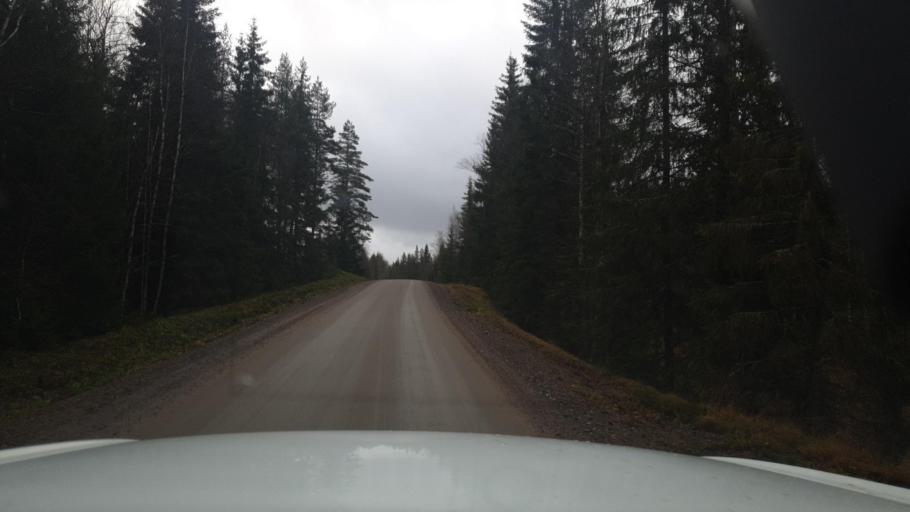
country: SE
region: Vaermland
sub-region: Eda Kommun
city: Charlottenberg
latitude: 60.0531
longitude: 12.5634
